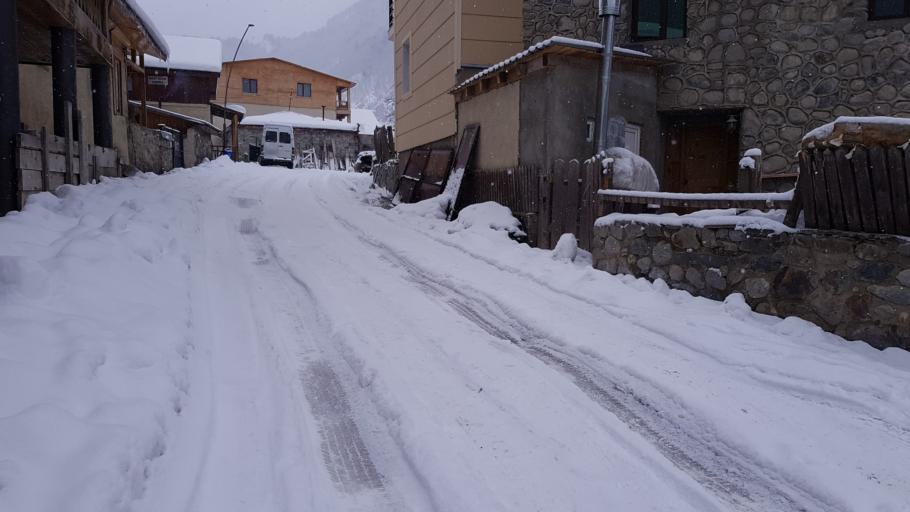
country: GE
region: Samegrelo and Zemo Svaneti
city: Mest'ia
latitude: 43.0429
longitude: 42.7272
